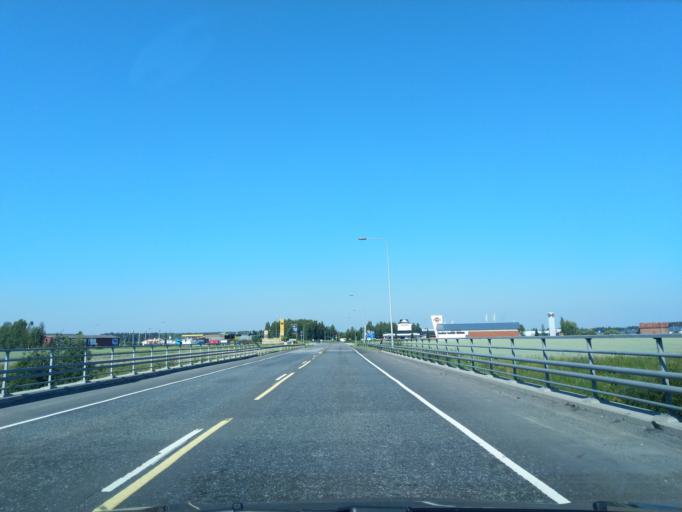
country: FI
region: Satakunta
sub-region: Pori
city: Huittinen
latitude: 61.1682
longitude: 22.6887
